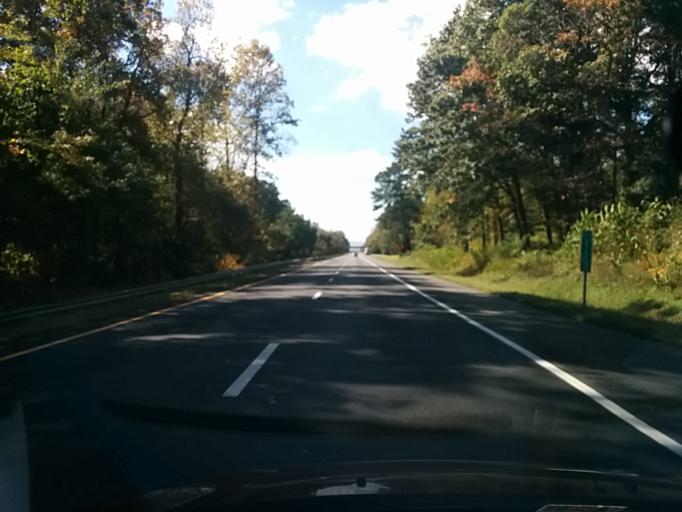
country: US
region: Virginia
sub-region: Albemarle County
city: Crozet
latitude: 38.0343
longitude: -78.6284
